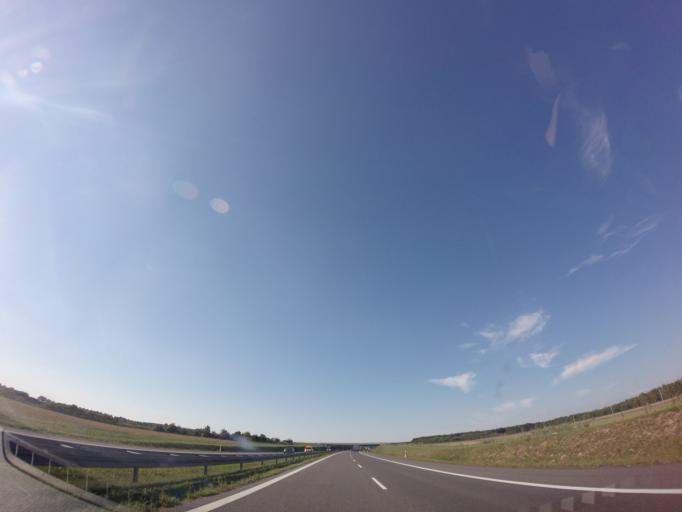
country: PL
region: Lubusz
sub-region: Powiat miedzyrzecki
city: Miedzyrzecz
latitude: 52.3710
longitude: 15.5465
